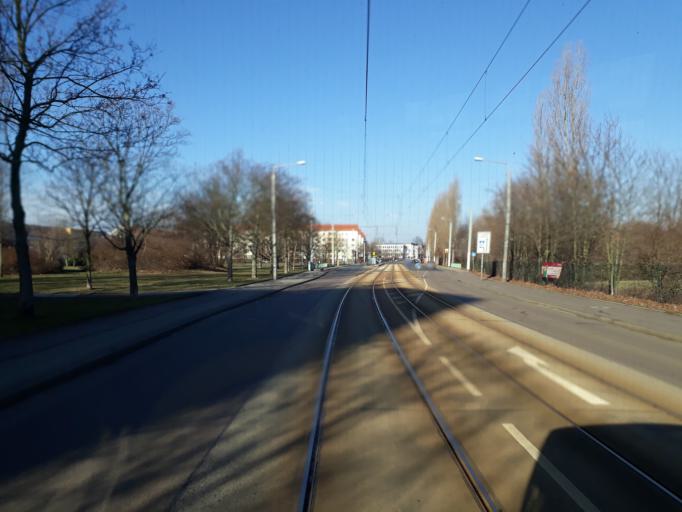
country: DE
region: Saxony
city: Heidenau
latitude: 51.0146
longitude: 13.8183
